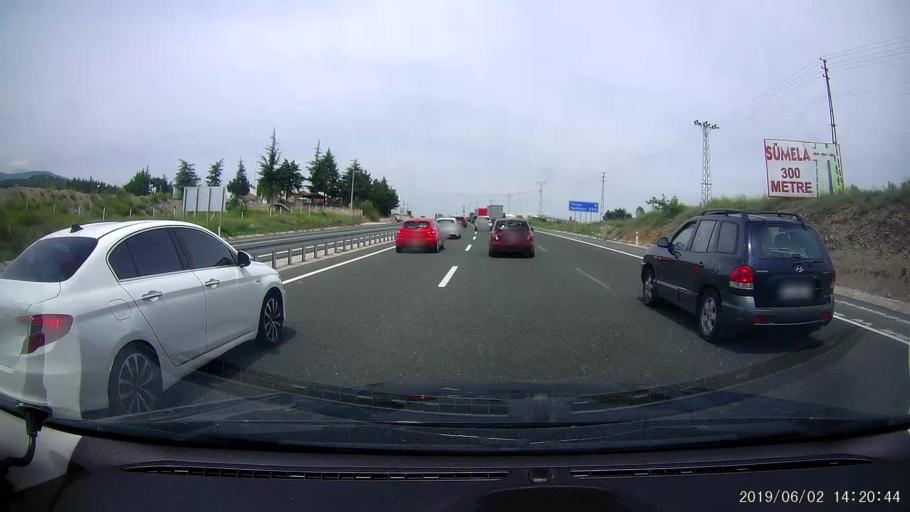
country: TR
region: Kastamonu
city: Tosya
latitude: 40.9726
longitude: 33.9964
